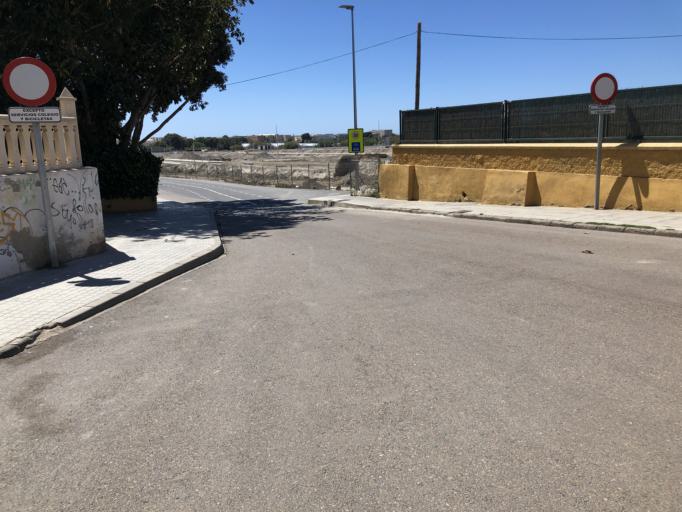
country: ES
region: Andalusia
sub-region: Provincia de Almeria
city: Almeria
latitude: 36.8381
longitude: -2.4054
